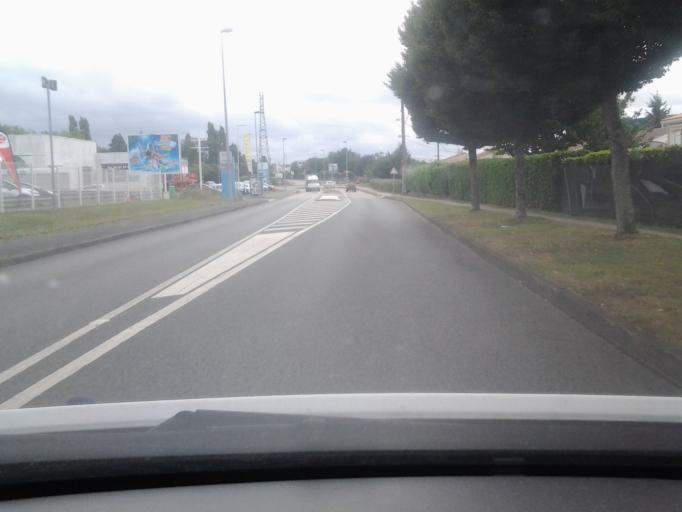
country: FR
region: Pays de la Loire
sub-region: Departement de la Vendee
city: La Roche-sur-Yon
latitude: 46.6518
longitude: -1.4336
